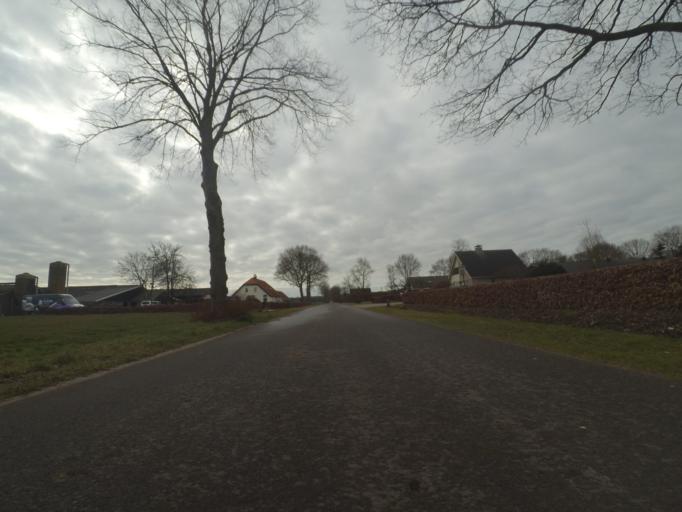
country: NL
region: Utrecht
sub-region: Gemeente Utrechtse Heuvelrug
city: Overberg
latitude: 52.0355
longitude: 5.5010
